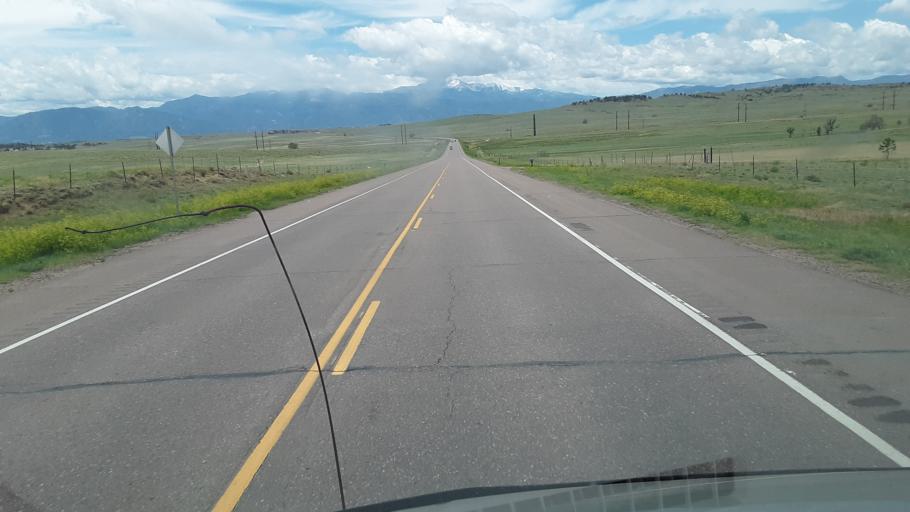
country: US
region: Colorado
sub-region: El Paso County
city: Cimarron Hills
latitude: 38.8388
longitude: -104.6131
